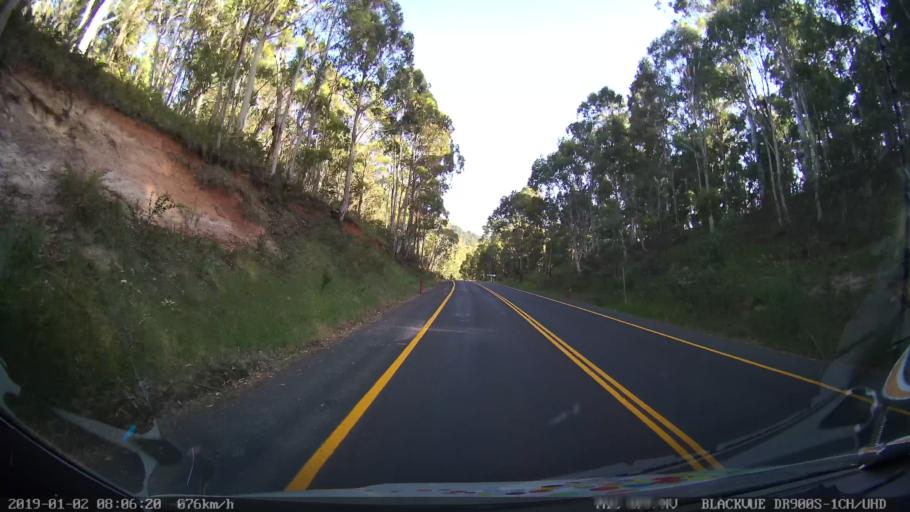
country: AU
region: New South Wales
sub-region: Tumut Shire
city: Tumut
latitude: -35.6411
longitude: 148.3872
